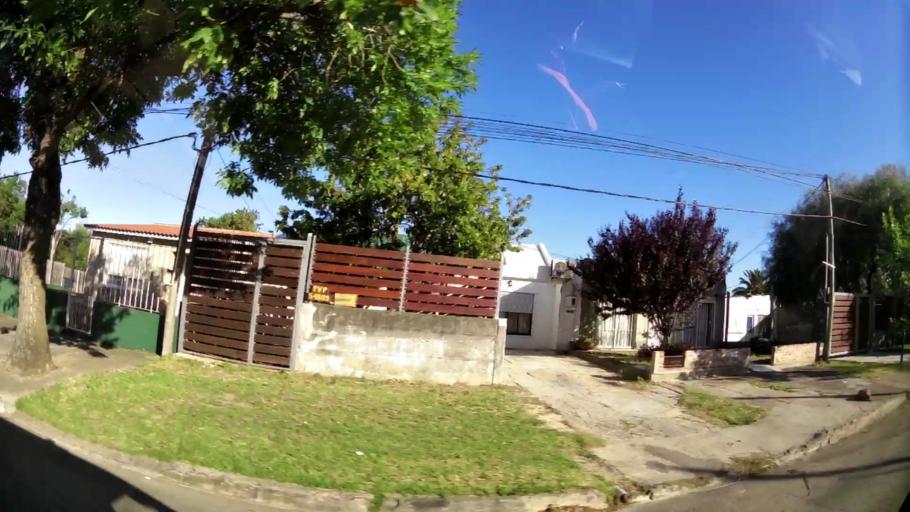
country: UY
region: Montevideo
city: Montevideo
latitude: -34.8325
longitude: -56.2056
